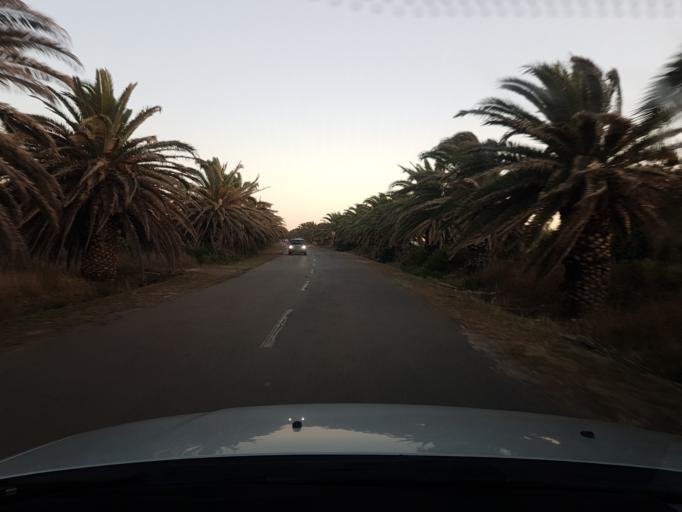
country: IT
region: Sardinia
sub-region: Provincia di Oristano
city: Riola Sardo
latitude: 40.0383
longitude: 8.4005
